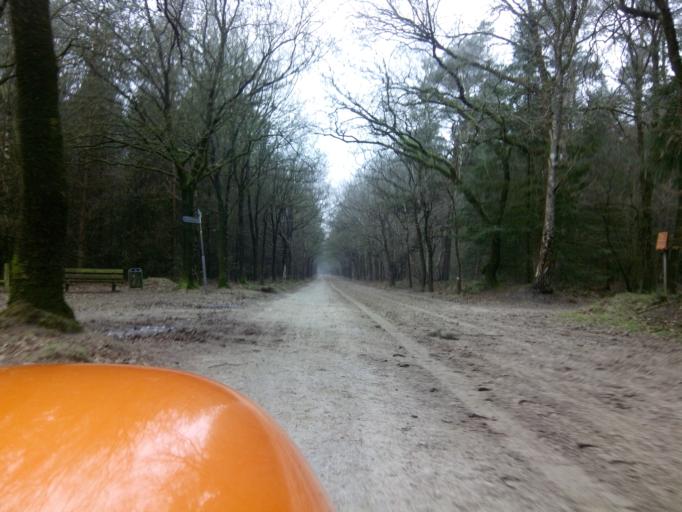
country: NL
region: Gelderland
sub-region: Gemeente Barneveld
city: Voorthuizen
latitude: 52.2185
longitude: 5.6328
